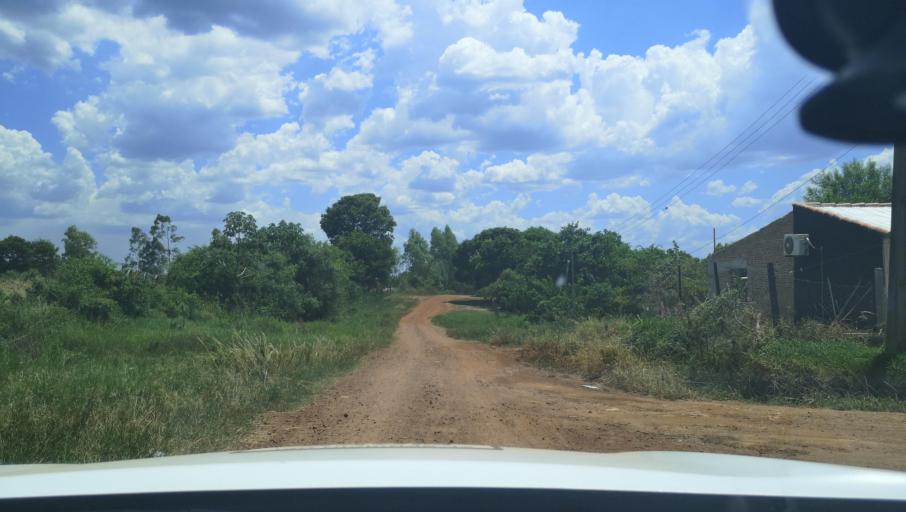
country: PY
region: Itapua
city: Carmen del Parana
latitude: -27.1725
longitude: -56.2460
